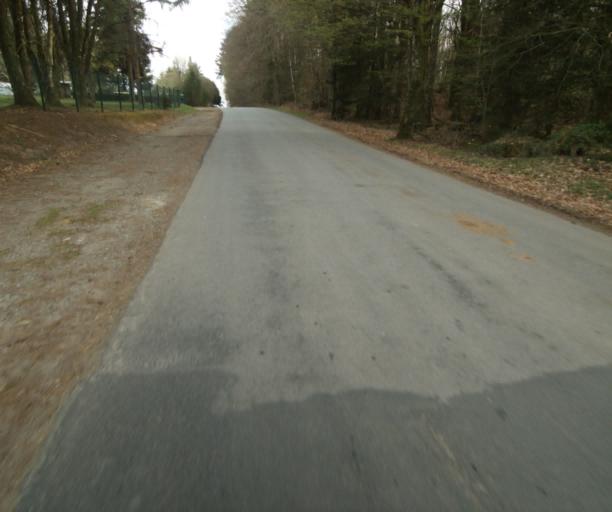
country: FR
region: Limousin
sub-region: Departement de la Correze
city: Naves
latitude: 45.3290
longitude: 1.7542
